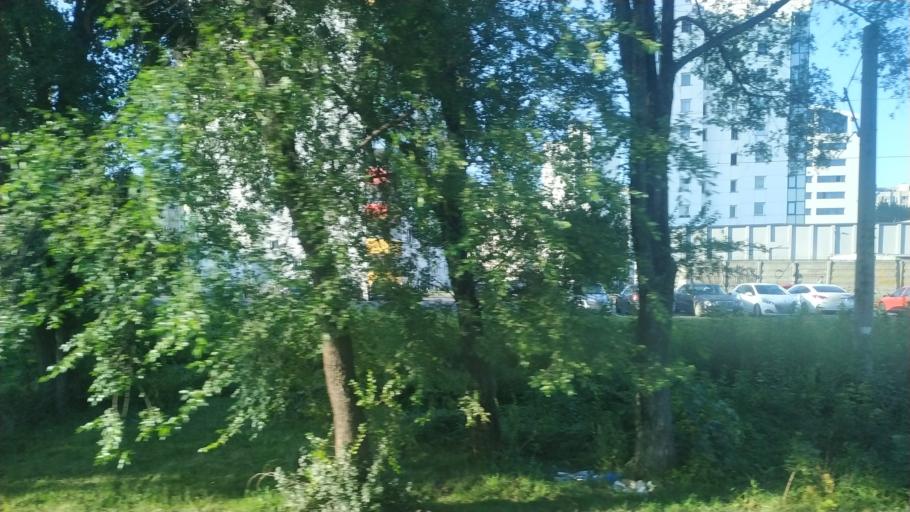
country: RO
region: Brasov
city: Brasov
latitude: 45.6606
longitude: 25.6211
